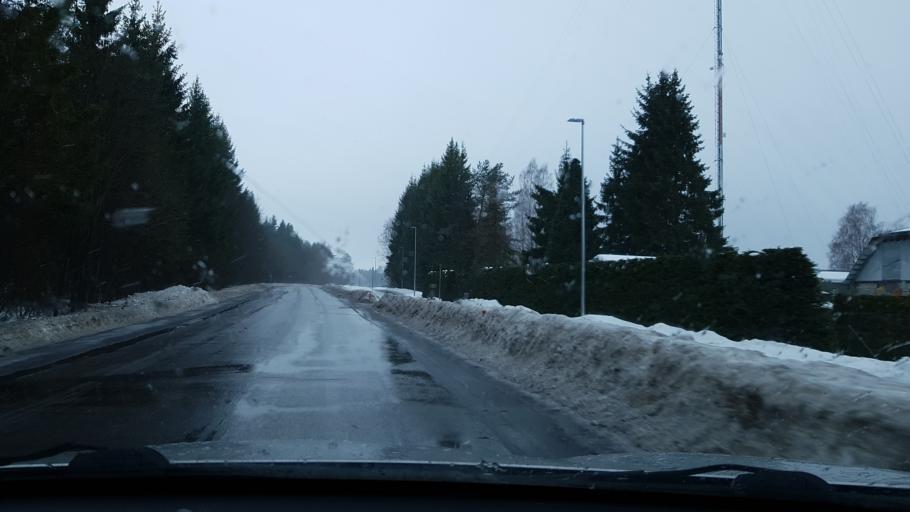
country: EE
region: Raplamaa
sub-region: Kohila vald
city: Kohila
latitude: 59.1700
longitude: 24.7332
